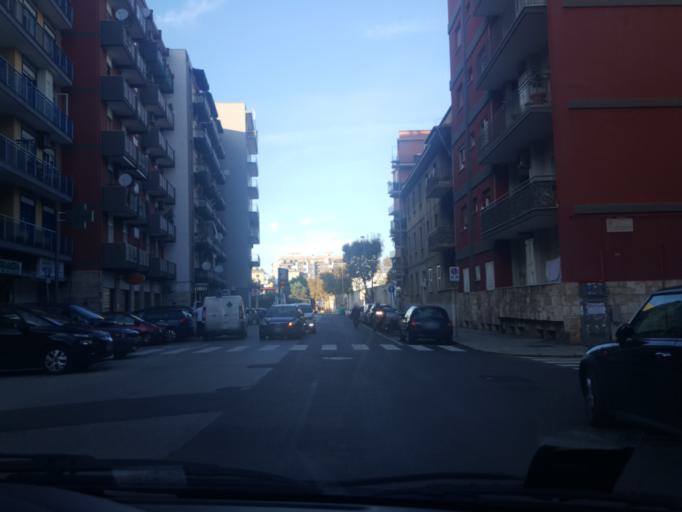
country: IT
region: Apulia
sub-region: Provincia di Bari
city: Bari
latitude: 41.1046
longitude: 16.8676
